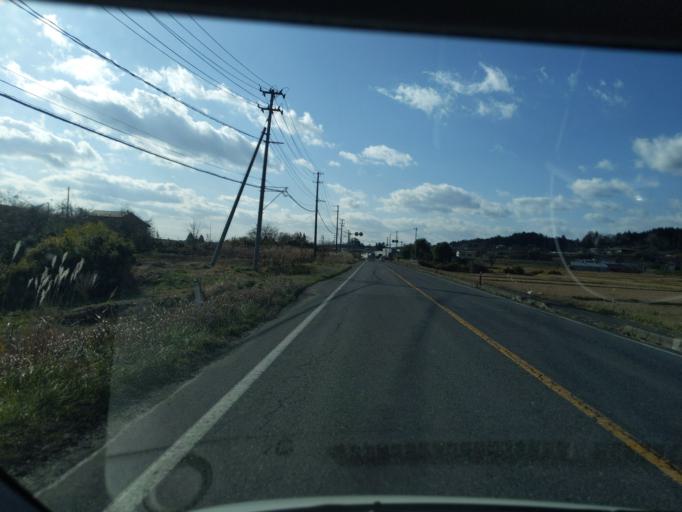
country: JP
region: Iwate
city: Ichinoseki
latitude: 38.8197
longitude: 141.0777
